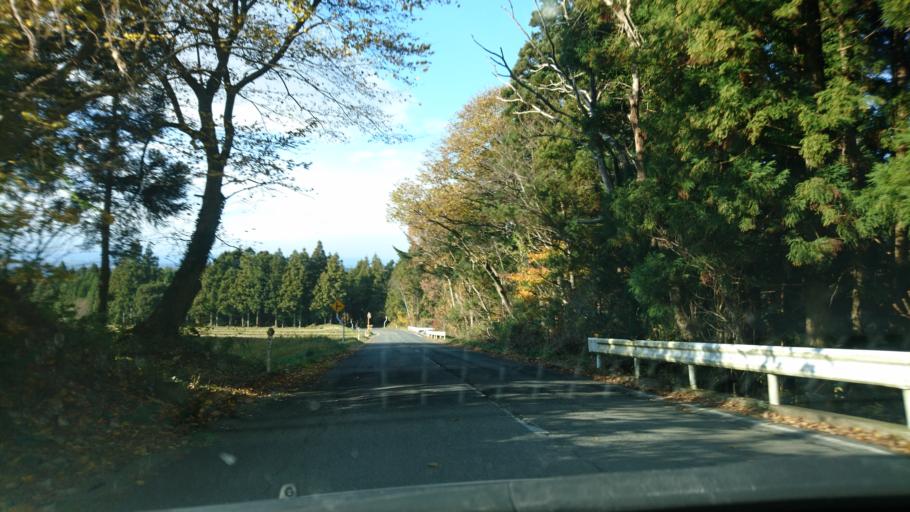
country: JP
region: Iwate
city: Mizusawa
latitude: 39.0312
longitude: 141.1612
